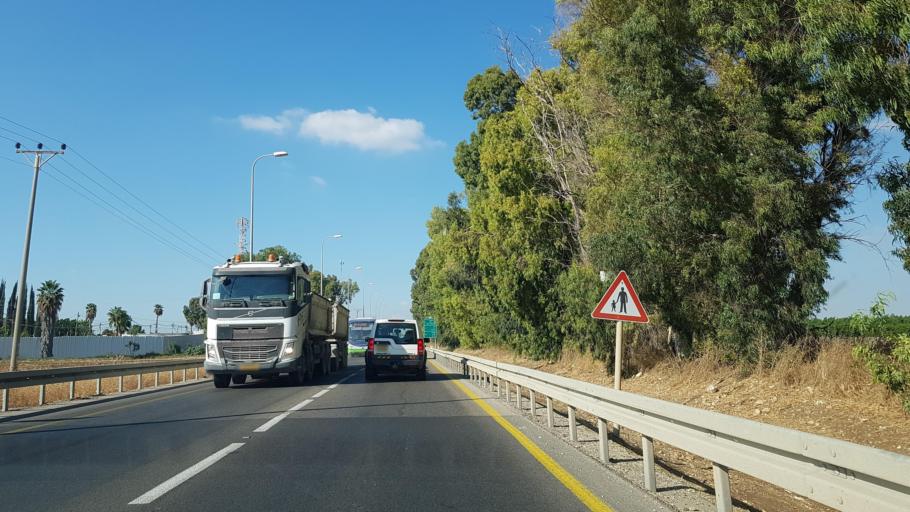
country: PS
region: West Bank
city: Tulkarm
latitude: 32.3141
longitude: 34.9993
